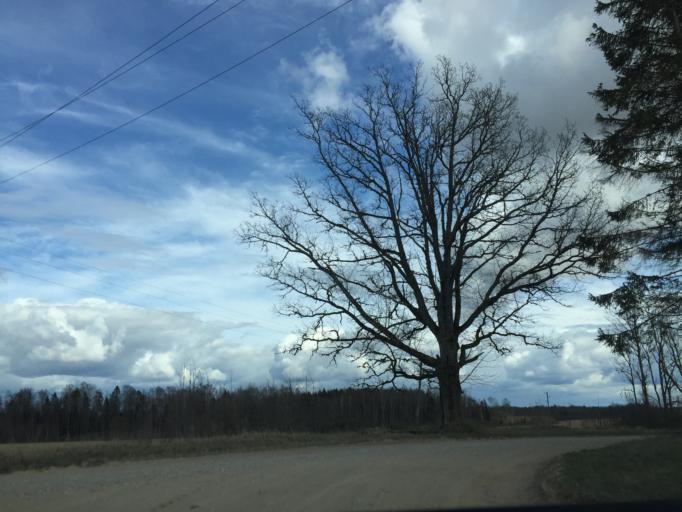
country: LV
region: Limbazu Rajons
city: Limbazi
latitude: 57.6173
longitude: 24.7765
